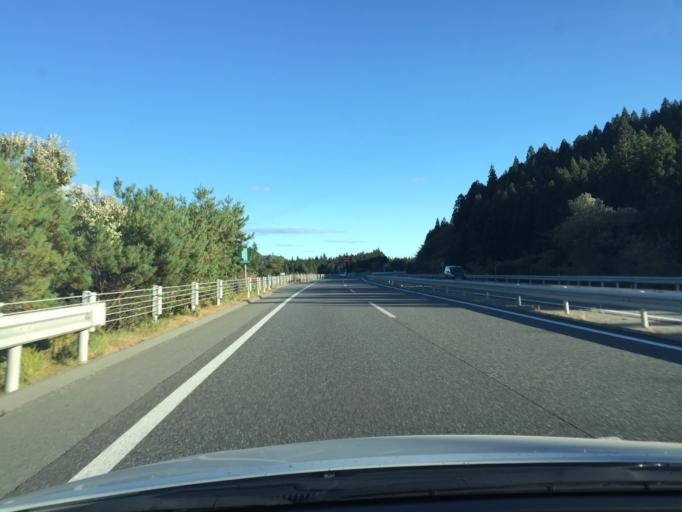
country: JP
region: Fukushima
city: Iwaki
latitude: 37.1069
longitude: 140.7642
